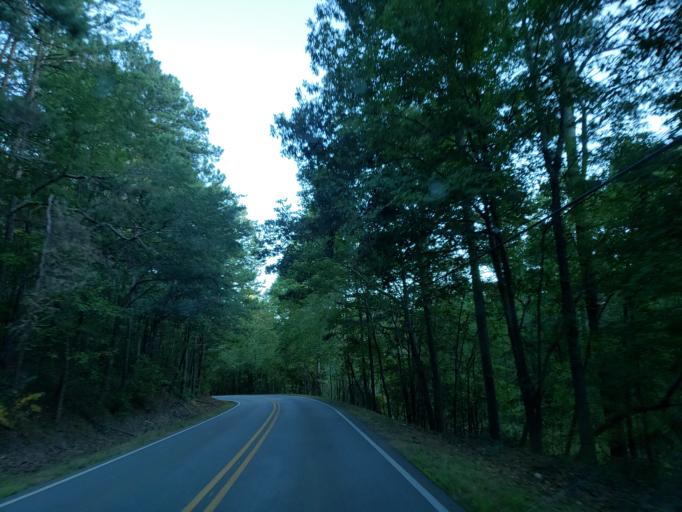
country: US
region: Georgia
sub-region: Bartow County
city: Rydal
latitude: 34.3887
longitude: -84.5936
